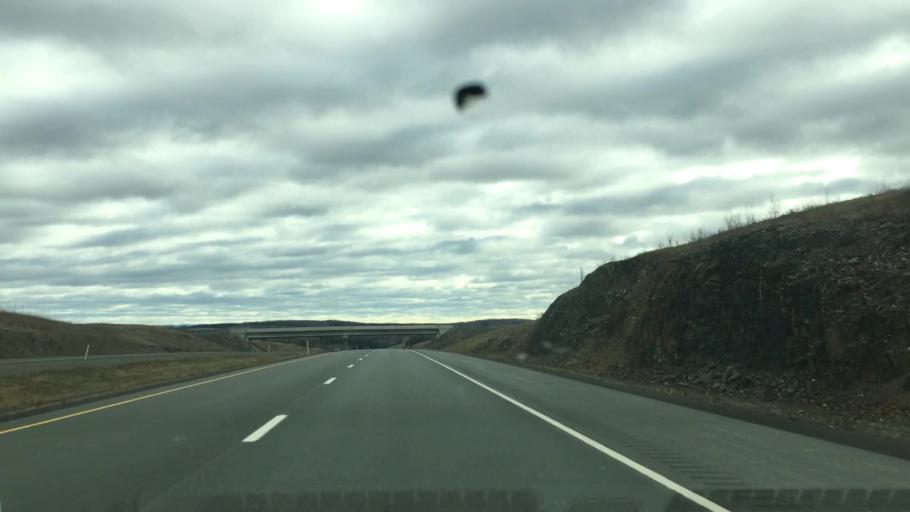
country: CA
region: New Brunswick
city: Florenceville-Bristol
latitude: 46.5491
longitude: -67.7306
